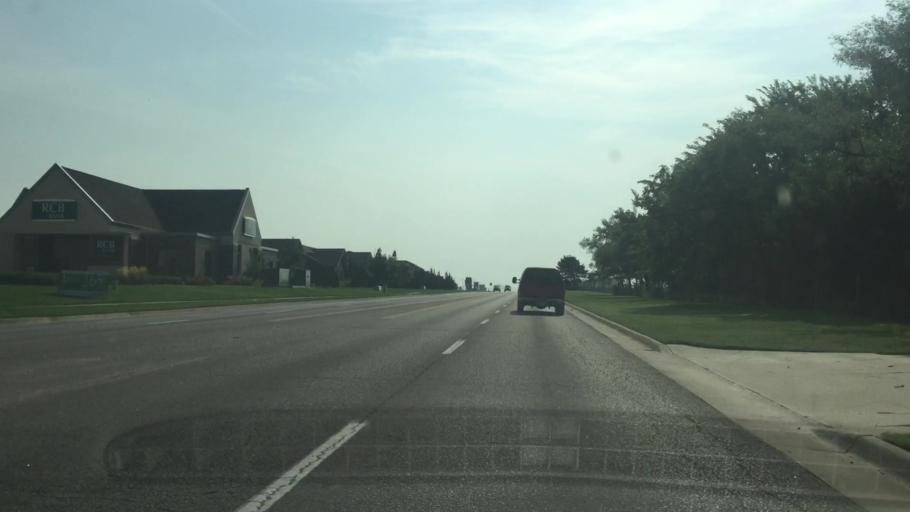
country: US
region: Kansas
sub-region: Sedgwick County
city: Bellaire
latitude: 37.7084
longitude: -97.2161
